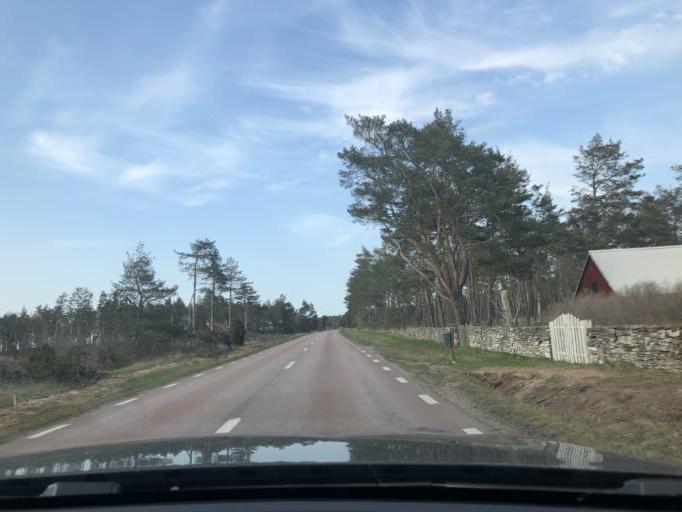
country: SE
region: Kalmar
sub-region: Morbylanga Kommun
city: Sodra Sandby
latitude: 56.5811
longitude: 16.6215
